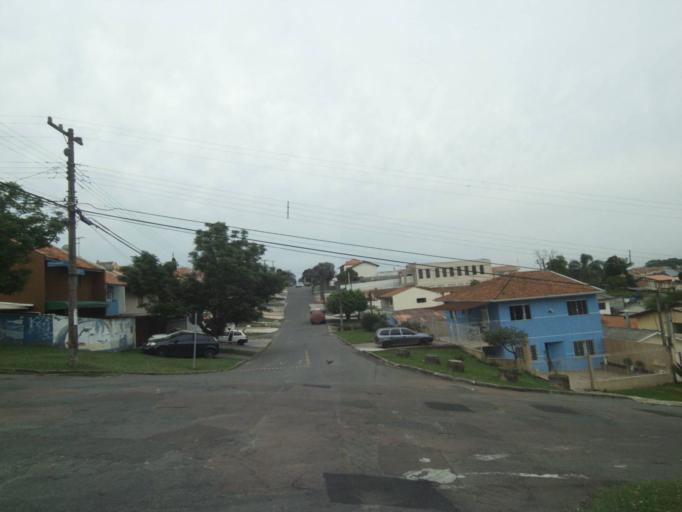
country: BR
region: Parana
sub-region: Pinhais
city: Pinhais
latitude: -25.3999
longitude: -49.2058
